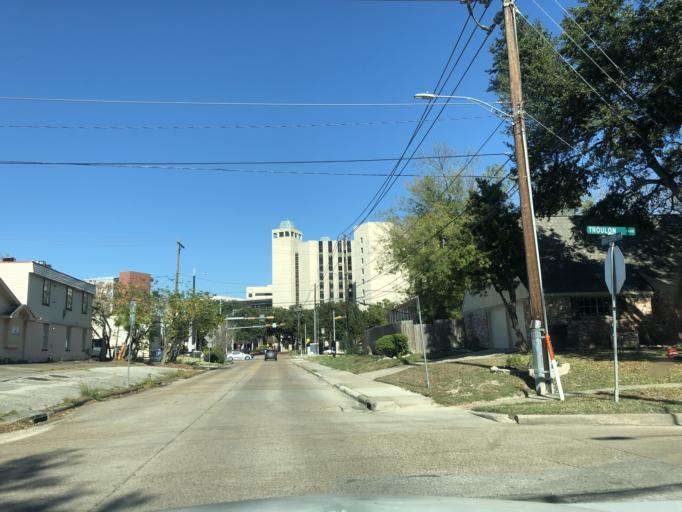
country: US
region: Texas
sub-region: Harris County
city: Bellaire
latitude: 29.6906
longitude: -95.5219
